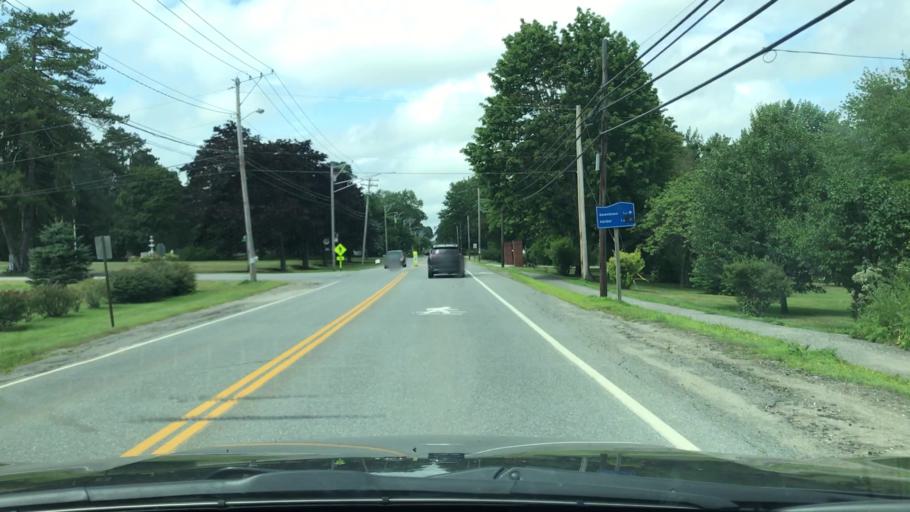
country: US
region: Maine
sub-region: Waldo County
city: Belfast
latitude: 44.4140
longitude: -68.9958
